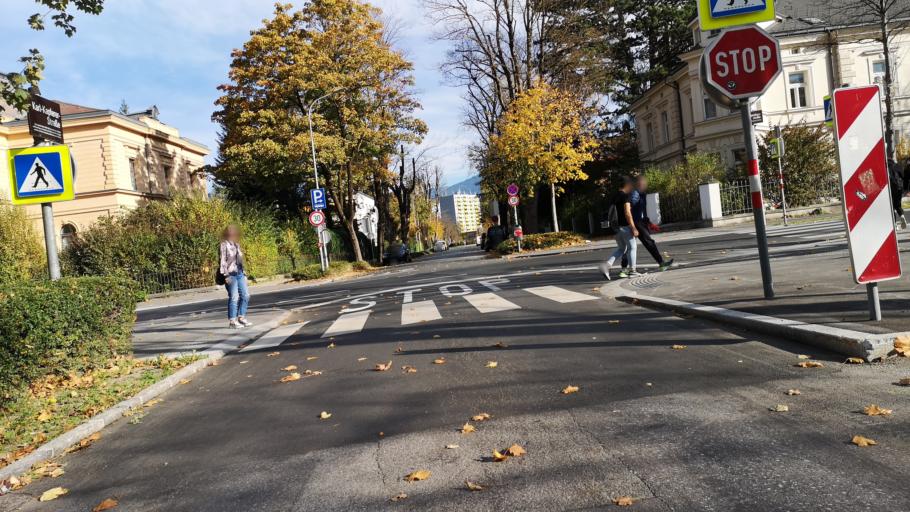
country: AT
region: Tyrol
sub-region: Innsbruck Stadt
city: Innsbruck
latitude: 47.2729
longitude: 11.4002
